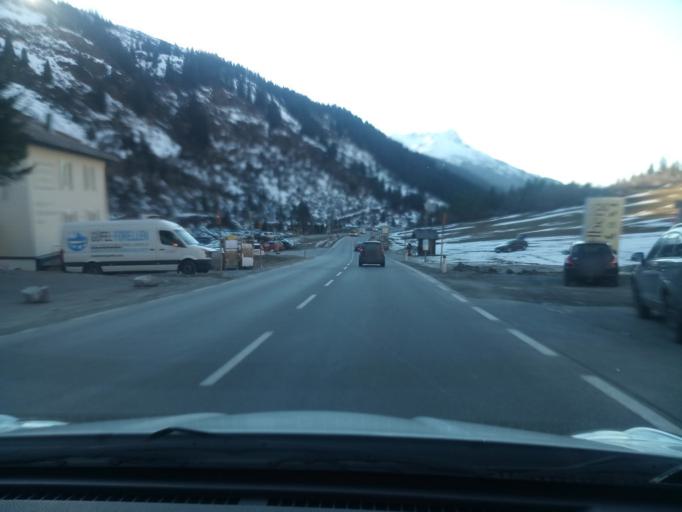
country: AT
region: Vorarlberg
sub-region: Politischer Bezirk Bludenz
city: Lech
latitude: 47.1400
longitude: 10.1586
